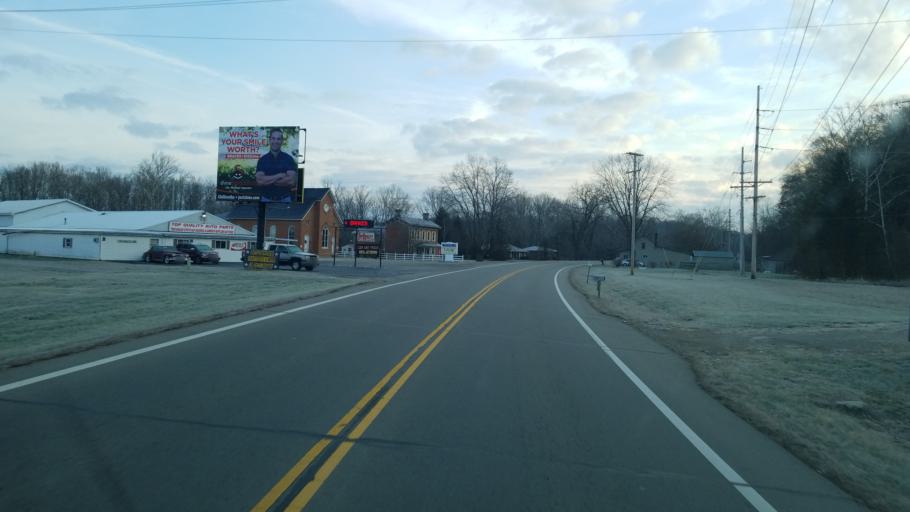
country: US
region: Ohio
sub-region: Ross County
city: North Fork Village
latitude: 39.3499
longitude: -83.0602
